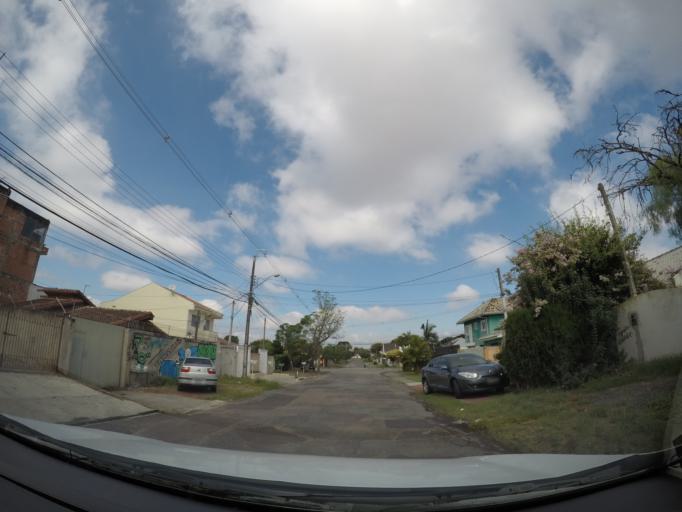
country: BR
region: Parana
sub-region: Sao Jose Dos Pinhais
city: Sao Jose dos Pinhais
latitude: -25.4925
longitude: -49.2226
